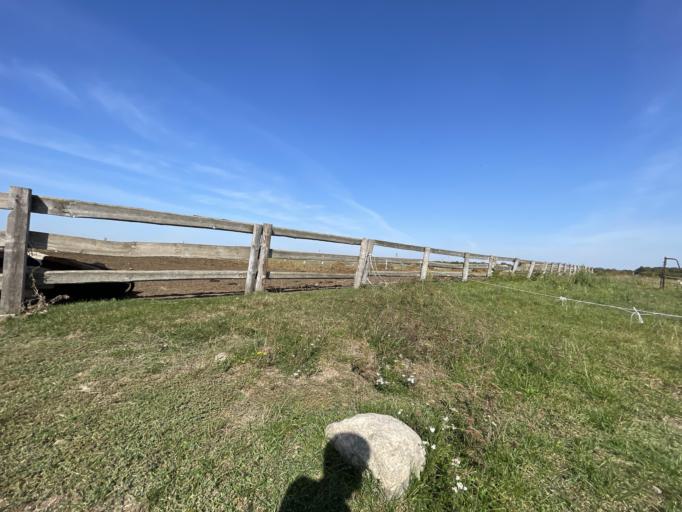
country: BY
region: Minsk
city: Kapyl'
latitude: 53.2546
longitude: 26.9405
